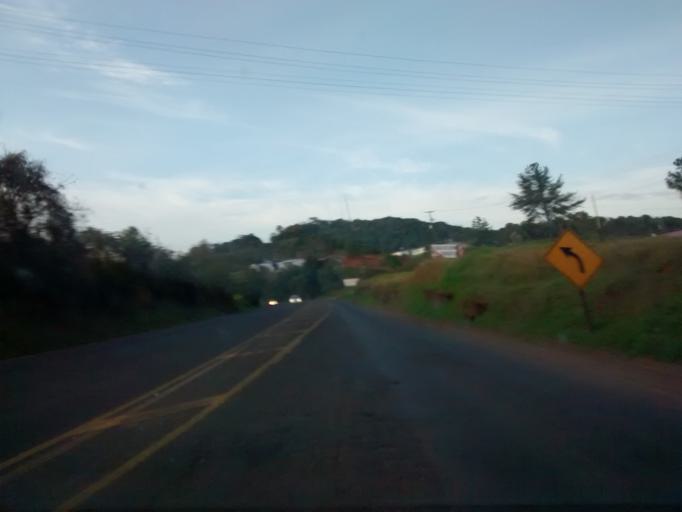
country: BR
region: Parana
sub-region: Francisco Beltrao
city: Francisco Beltrao
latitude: -26.1285
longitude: -53.0405
